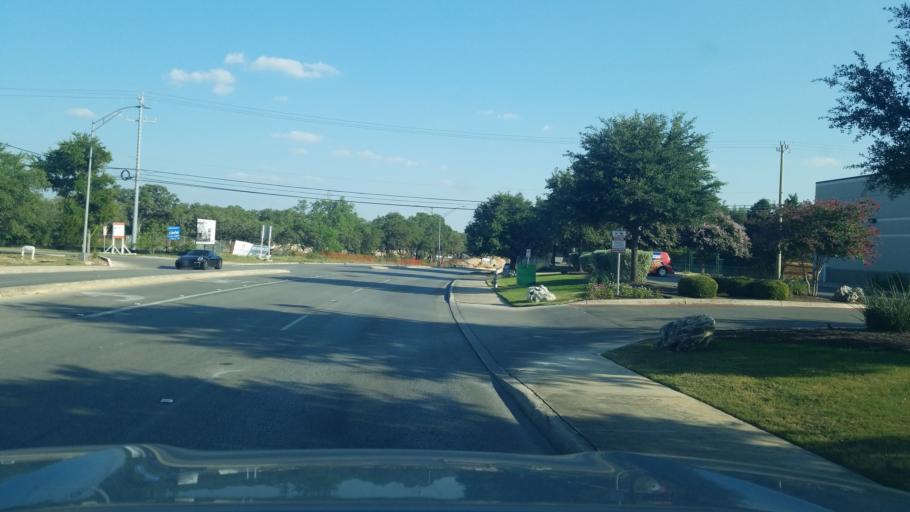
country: US
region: Texas
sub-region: Bexar County
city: Shavano Park
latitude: 29.6022
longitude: -98.5332
